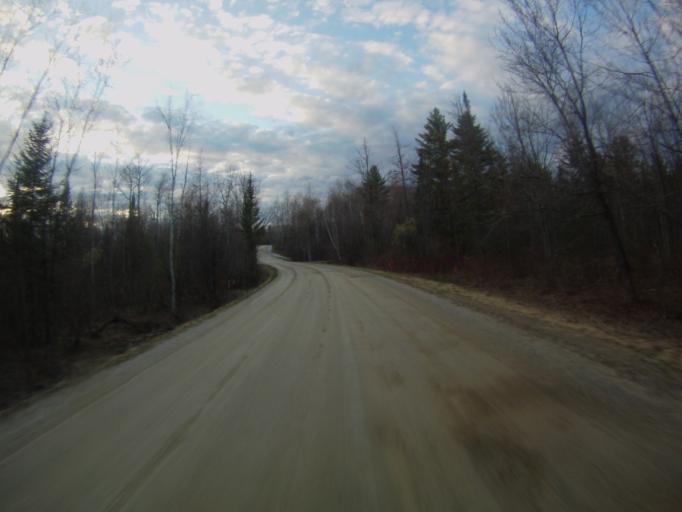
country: US
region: Vermont
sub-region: Rutland County
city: Brandon
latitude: 43.8990
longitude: -73.0142
